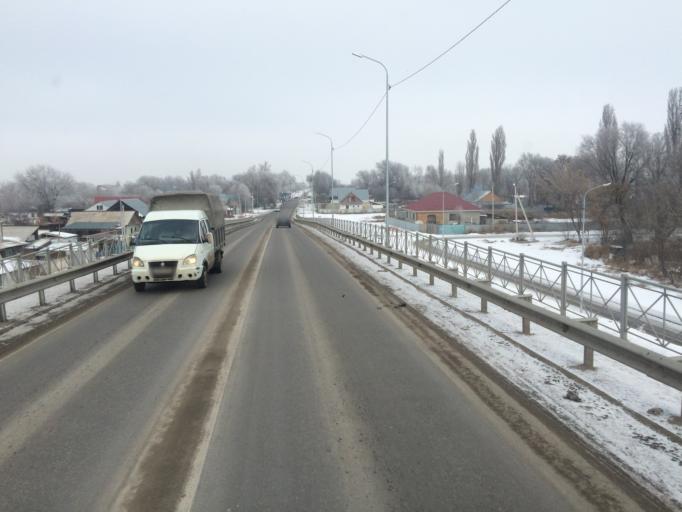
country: KZ
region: Almaty Oblysy
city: Burunday
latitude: 43.3638
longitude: 76.7261
